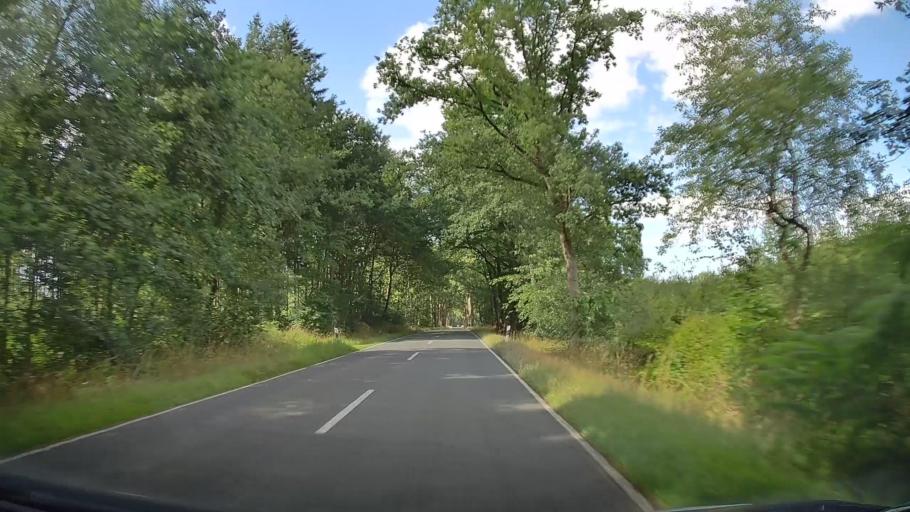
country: DE
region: Lower Saxony
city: Bippen
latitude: 52.5975
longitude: 7.7422
